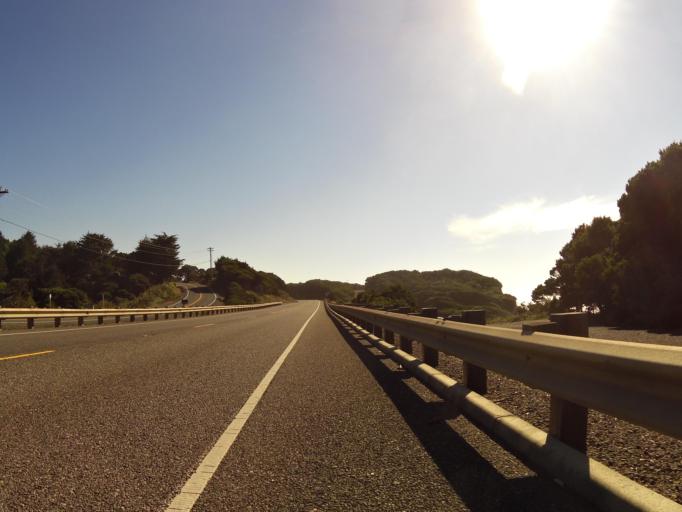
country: US
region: Oregon
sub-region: Curry County
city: Gold Beach
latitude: 42.5150
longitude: -124.4092
